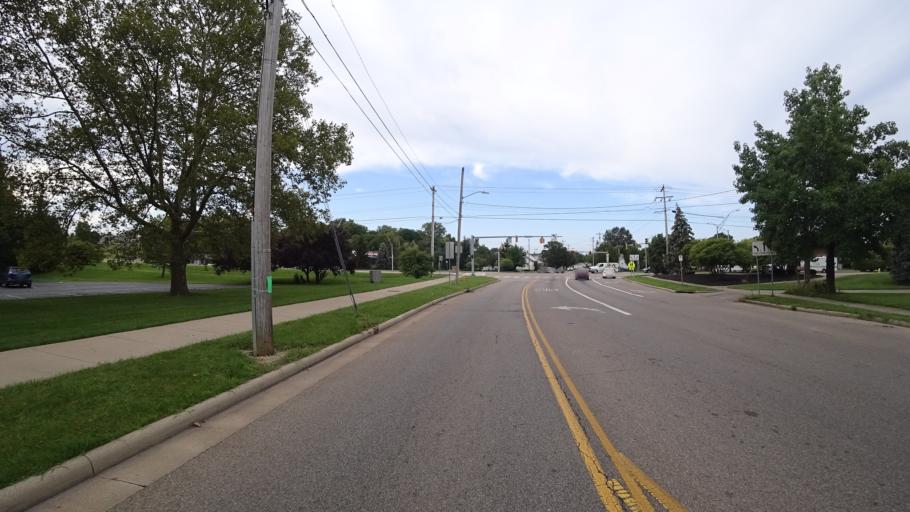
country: US
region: Ohio
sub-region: Butler County
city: Hamilton
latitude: 39.3938
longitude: -84.5427
